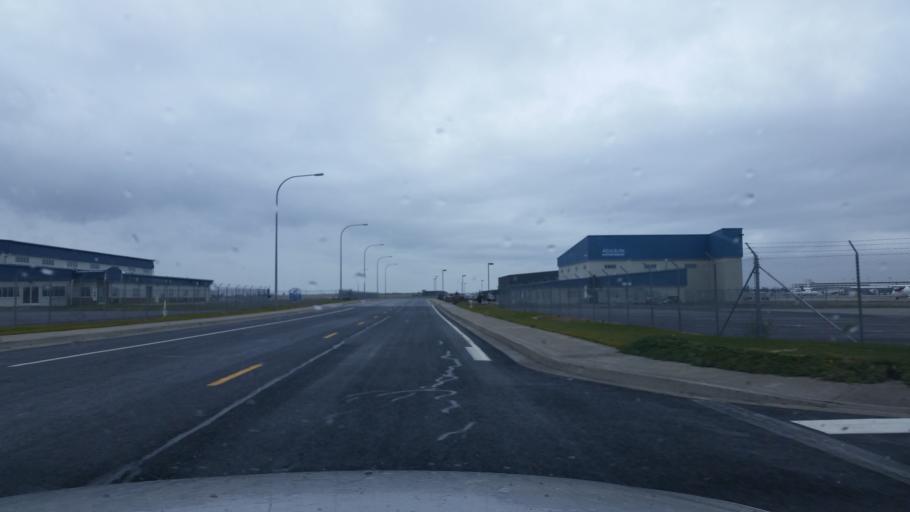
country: US
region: Washington
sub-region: Spokane County
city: Airway Heights
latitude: 47.6197
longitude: -117.5245
